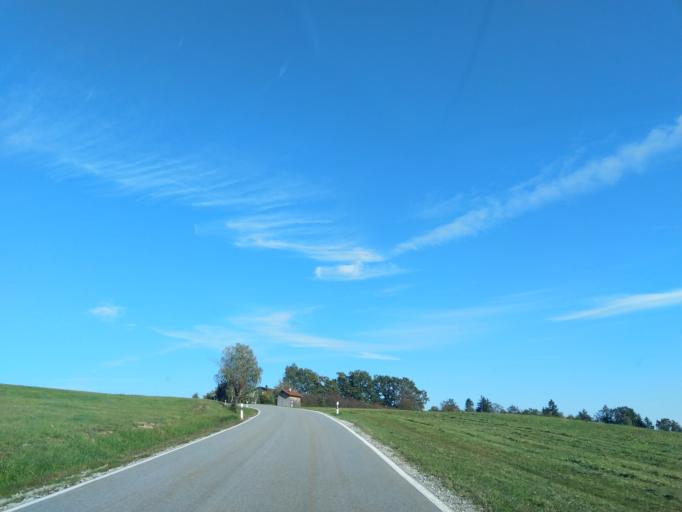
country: DE
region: Bavaria
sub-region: Lower Bavaria
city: Offenberg
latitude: 48.8888
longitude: 12.8407
